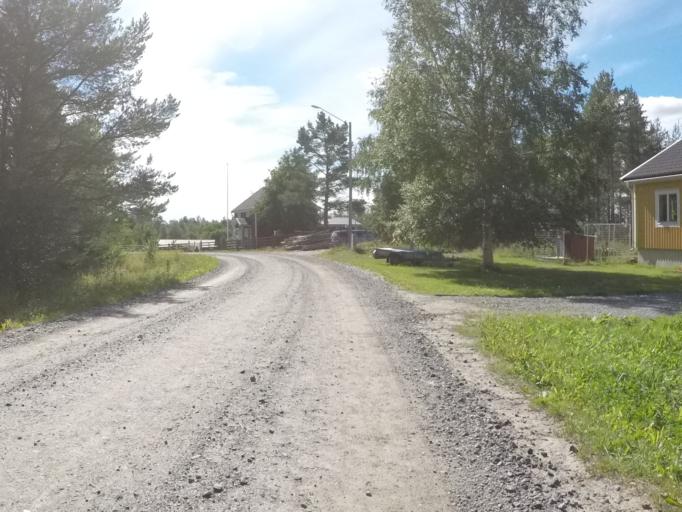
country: SE
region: Vaesterbotten
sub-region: Robertsfors Kommun
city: Robertsfors
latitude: 64.0016
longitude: 20.8109
